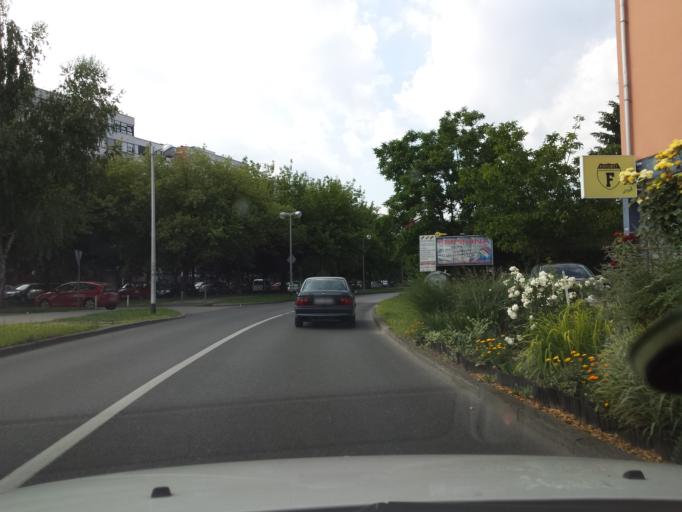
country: HR
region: Grad Zagreb
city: Jankomir
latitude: 45.8033
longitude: 15.8976
